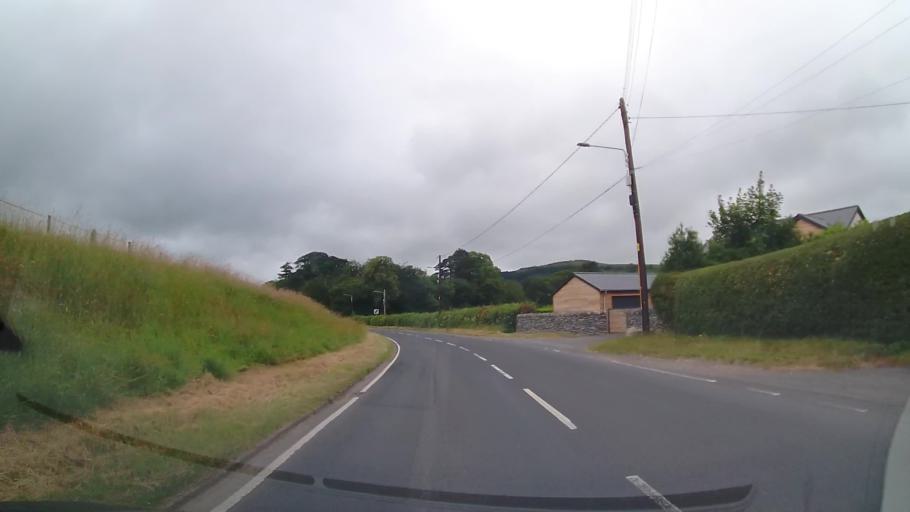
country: GB
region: Wales
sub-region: Denbighshire
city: Llandrillo
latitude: 52.9231
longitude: -3.4401
